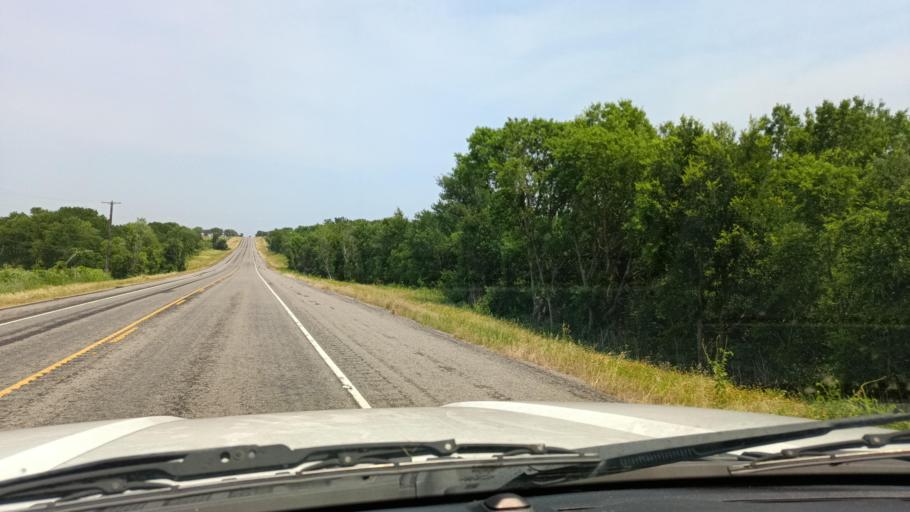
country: US
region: Texas
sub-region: Milam County
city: Cameron
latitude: 30.8549
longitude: -97.0996
